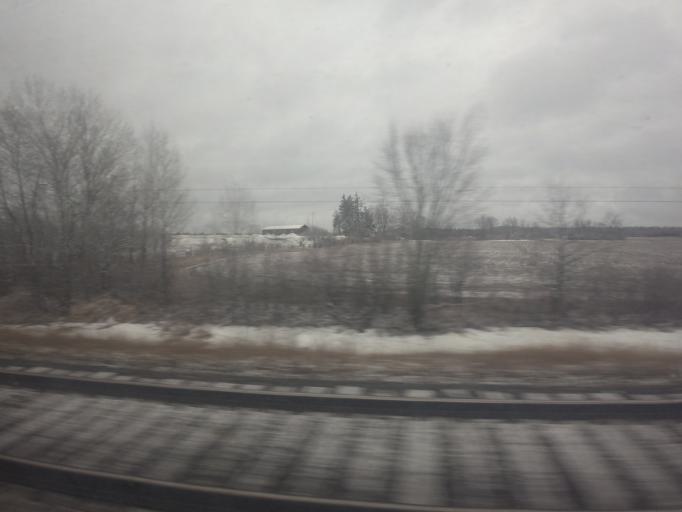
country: US
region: New York
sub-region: Jefferson County
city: Alexandria Bay
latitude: 44.3925
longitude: -76.0404
